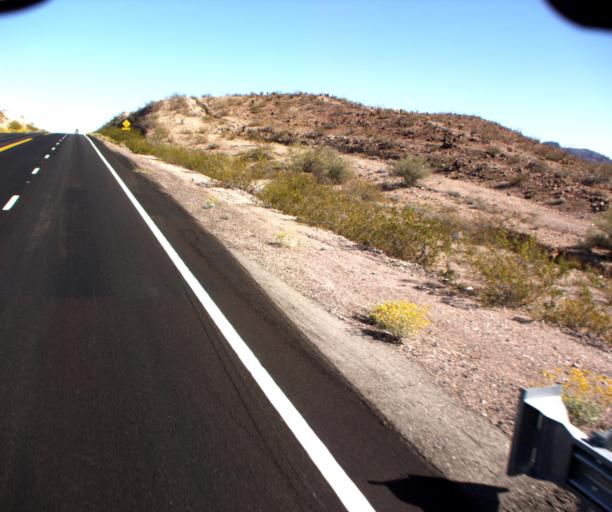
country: US
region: Arizona
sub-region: La Paz County
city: Quartzsite
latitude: 33.2405
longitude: -114.2486
